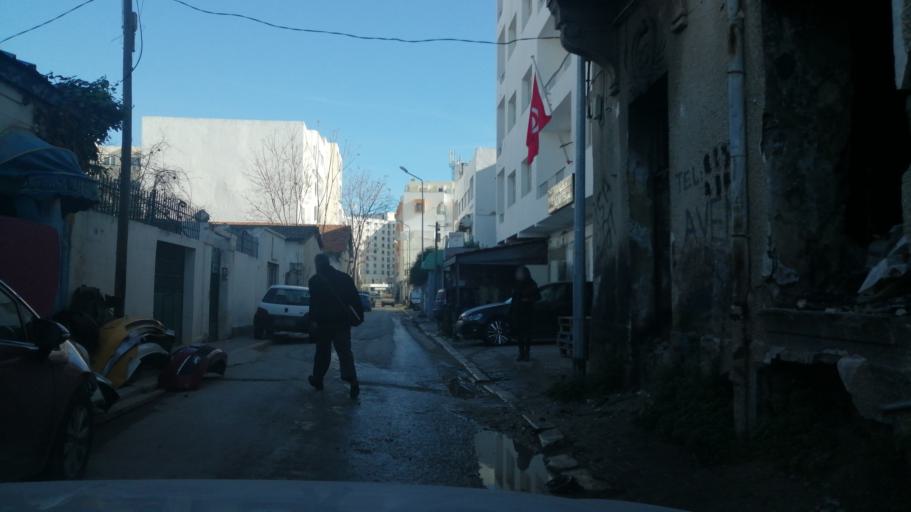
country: TN
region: Tunis
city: Tunis
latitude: 36.8113
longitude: 10.1719
